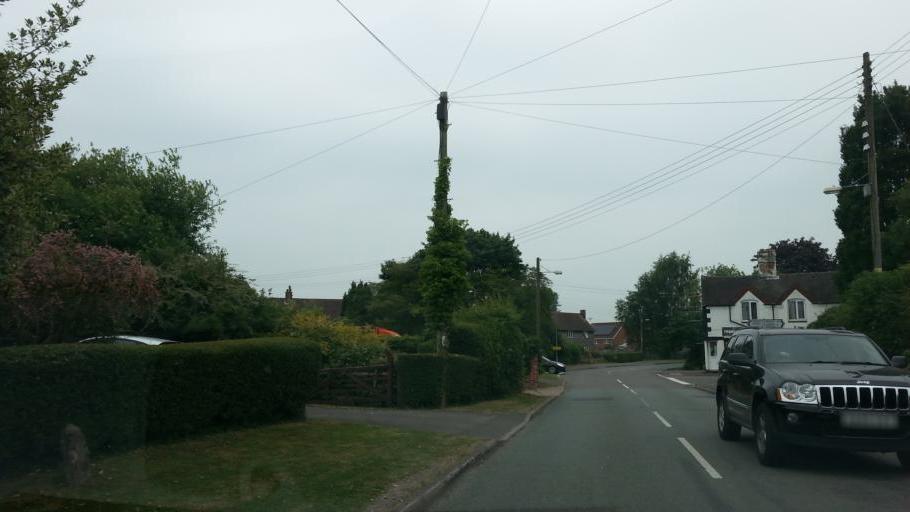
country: GB
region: England
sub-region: Staffordshire
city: Colwich
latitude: 52.8304
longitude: -1.9995
